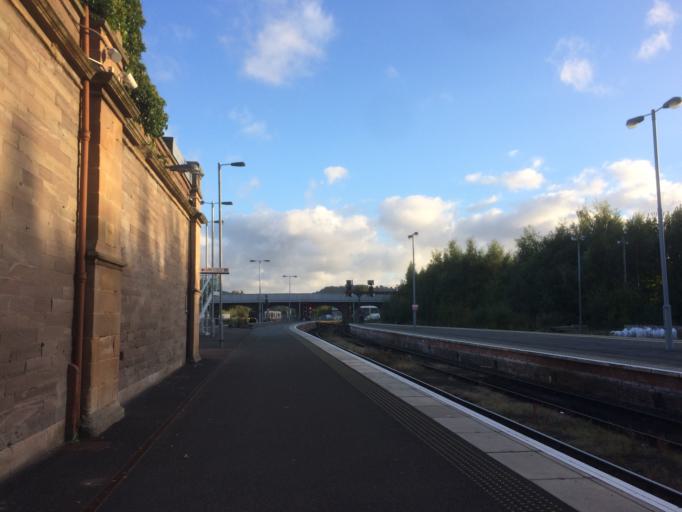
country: GB
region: Scotland
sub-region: Perth and Kinross
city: Perth
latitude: 56.3912
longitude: -3.4392
